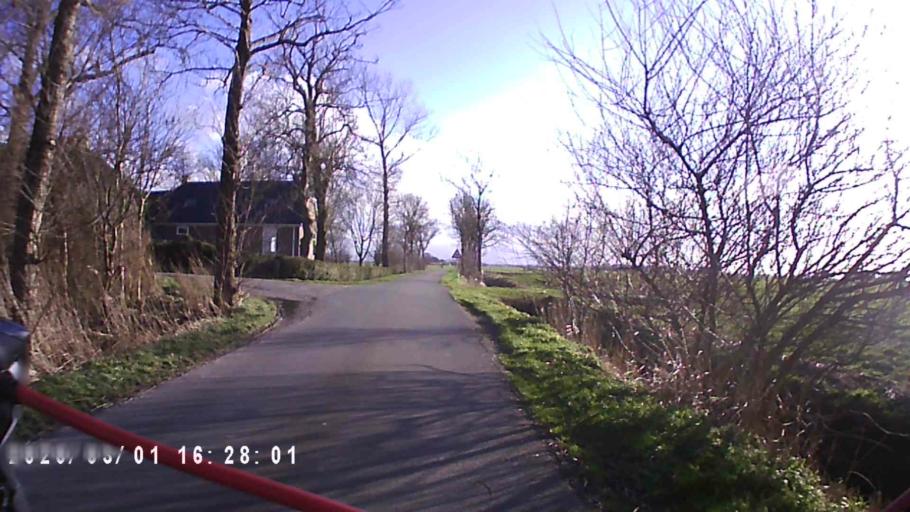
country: NL
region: Groningen
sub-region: Gemeente Zuidhorn
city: Oldehove
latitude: 53.3049
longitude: 6.4287
